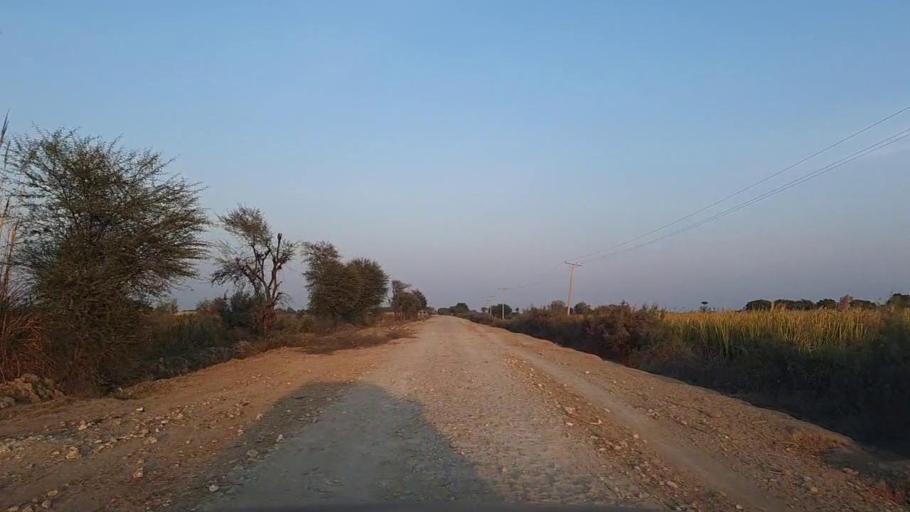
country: PK
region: Sindh
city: Tando Mittha Khan
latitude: 25.9711
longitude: 69.0883
